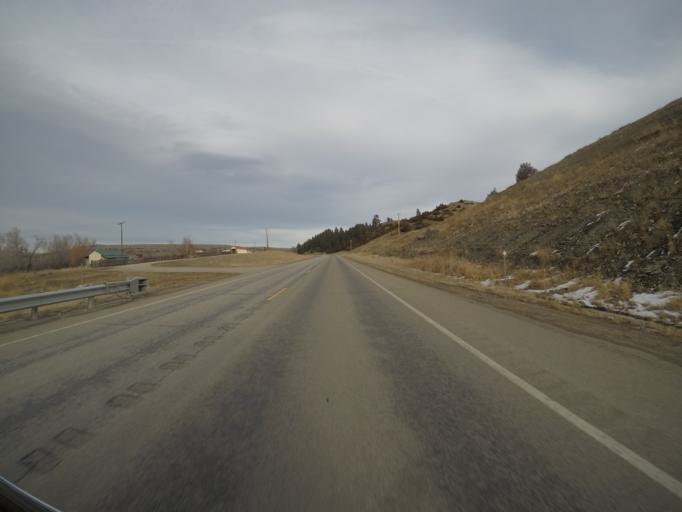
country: US
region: Montana
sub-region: Stillwater County
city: Absarokee
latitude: 45.5387
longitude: -109.4080
